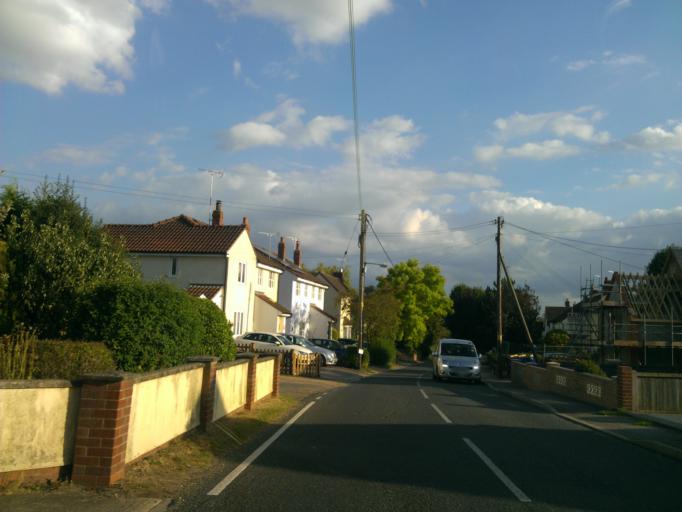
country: GB
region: England
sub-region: Essex
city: Rayne
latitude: 51.8578
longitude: 0.6018
